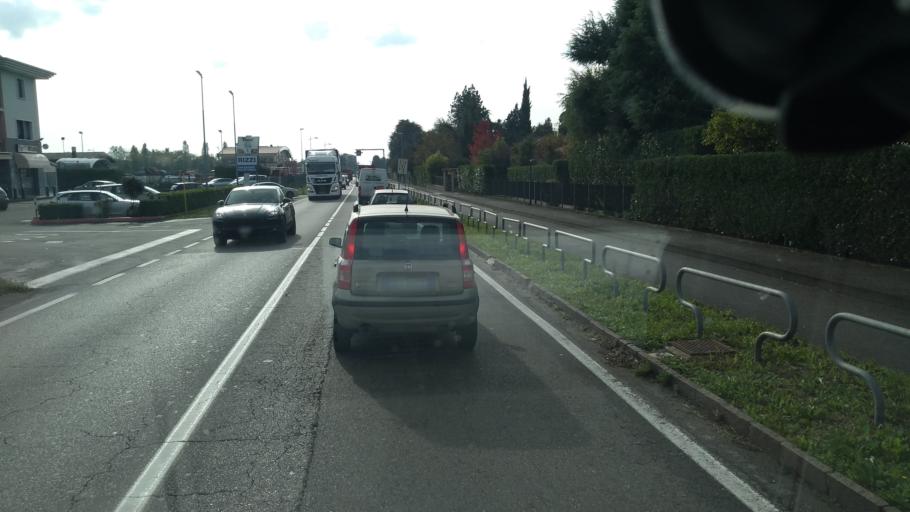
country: IT
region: Lombardy
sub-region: Provincia di Bergamo
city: Urgnano
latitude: 45.6059
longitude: 9.6968
